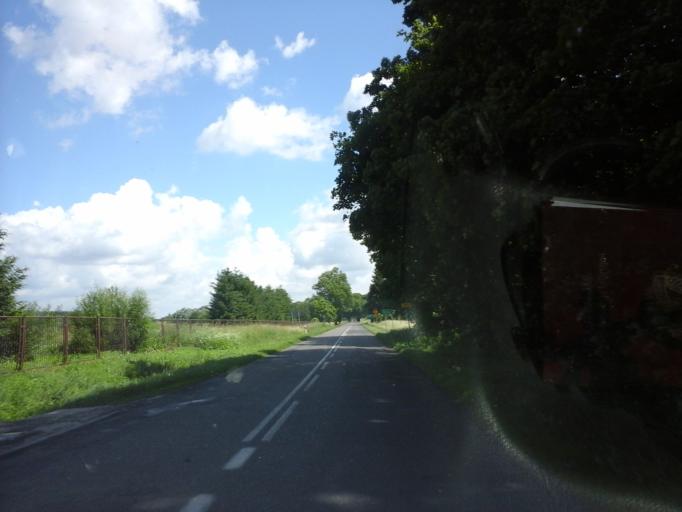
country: PL
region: West Pomeranian Voivodeship
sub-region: Powiat lobeski
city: Lobez
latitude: 53.6458
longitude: 15.6370
